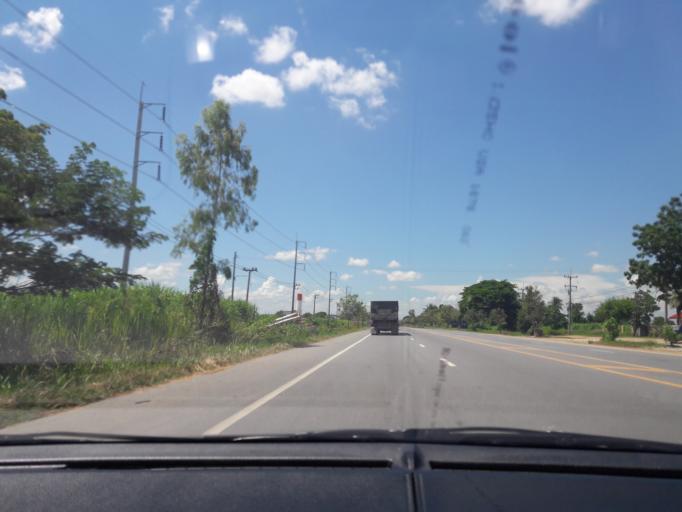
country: TH
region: Kanchanaburi
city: Phanom Thuan
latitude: 14.0469
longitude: 99.7823
